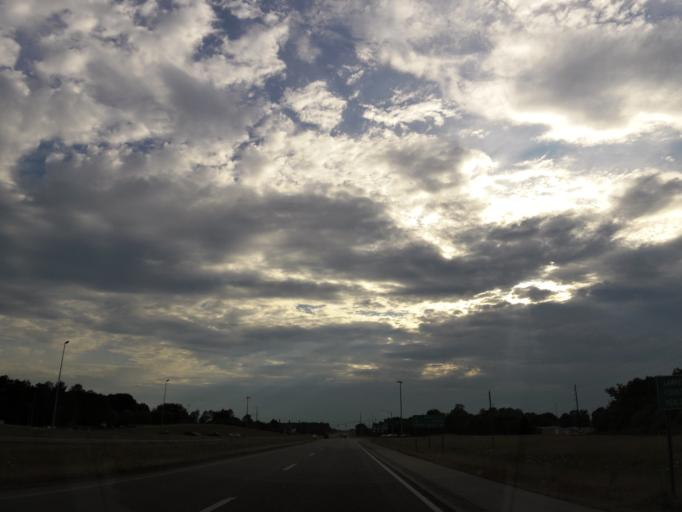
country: US
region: Alabama
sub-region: Lawrence County
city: Moulton
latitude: 34.4930
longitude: -87.2765
